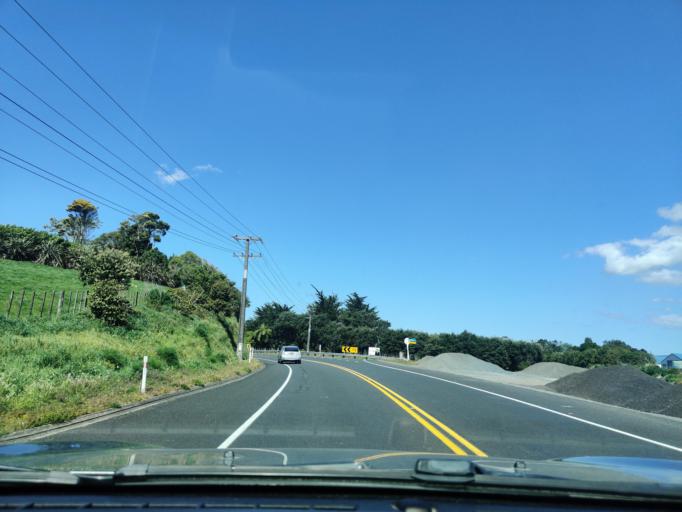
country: NZ
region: Taranaki
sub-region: New Plymouth District
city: New Plymouth
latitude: -39.1015
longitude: 174.0101
